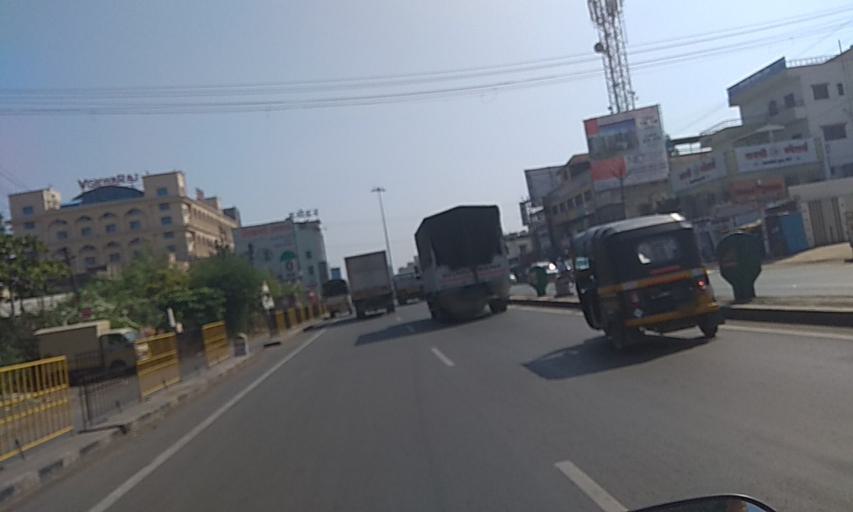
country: IN
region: Maharashtra
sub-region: Pune Division
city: Lohogaon
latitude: 18.4894
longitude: 74.0204
